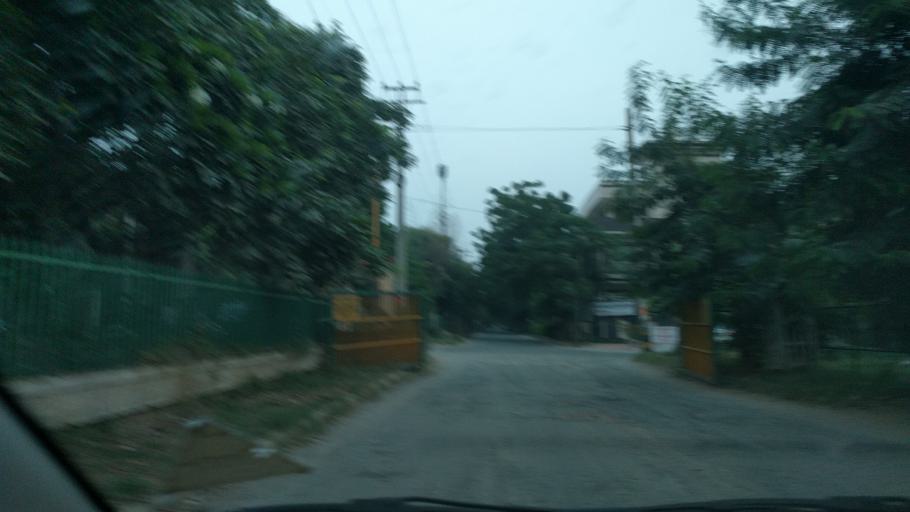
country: IN
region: Haryana
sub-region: Gurgaon
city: Gurgaon
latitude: 28.4522
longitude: 77.0604
